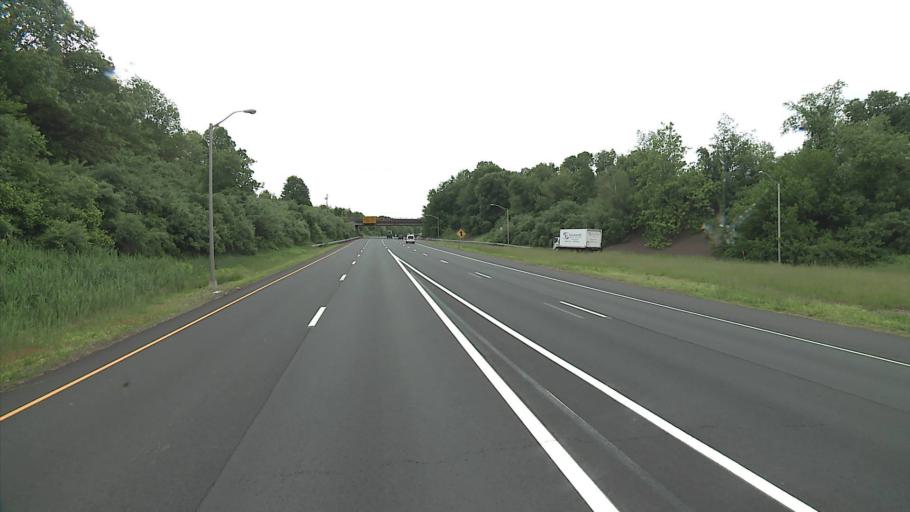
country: US
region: Connecticut
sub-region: Middlesex County
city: Cromwell
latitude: 41.6218
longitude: -72.6857
